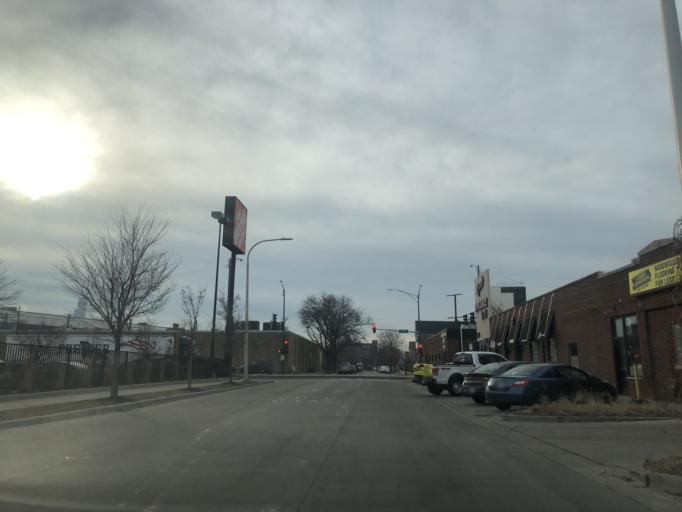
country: US
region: Illinois
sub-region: Cook County
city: Chicago
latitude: 41.9114
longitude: -87.6605
